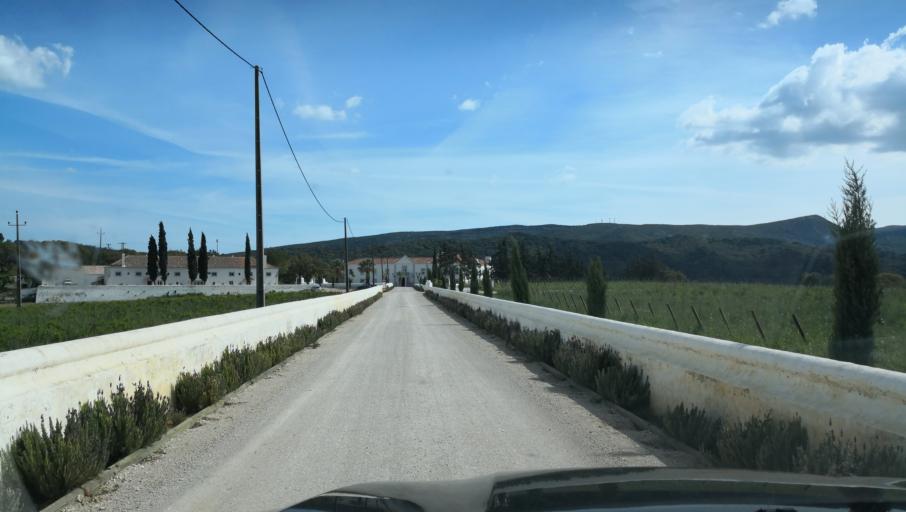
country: PT
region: Setubal
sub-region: Palmela
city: Quinta do Anjo
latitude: 38.5245
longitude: -8.9454
